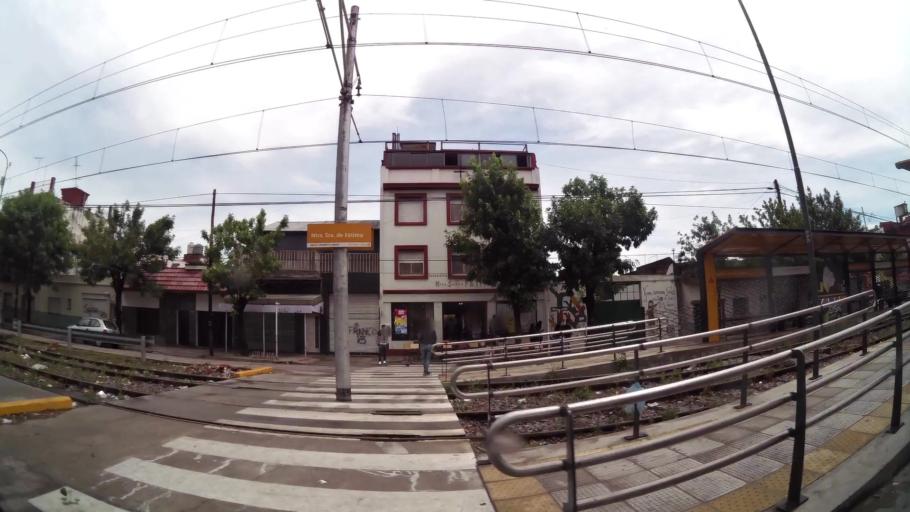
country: AR
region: Buenos Aires F.D.
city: Villa Lugano
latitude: -34.6605
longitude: -58.4486
